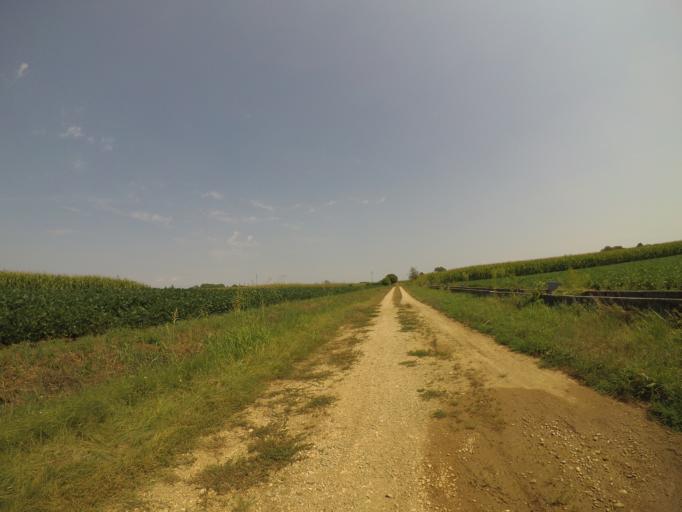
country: IT
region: Friuli Venezia Giulia
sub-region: Provincia di Udine
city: Talmassons
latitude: 45.9363
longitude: 13.1047
